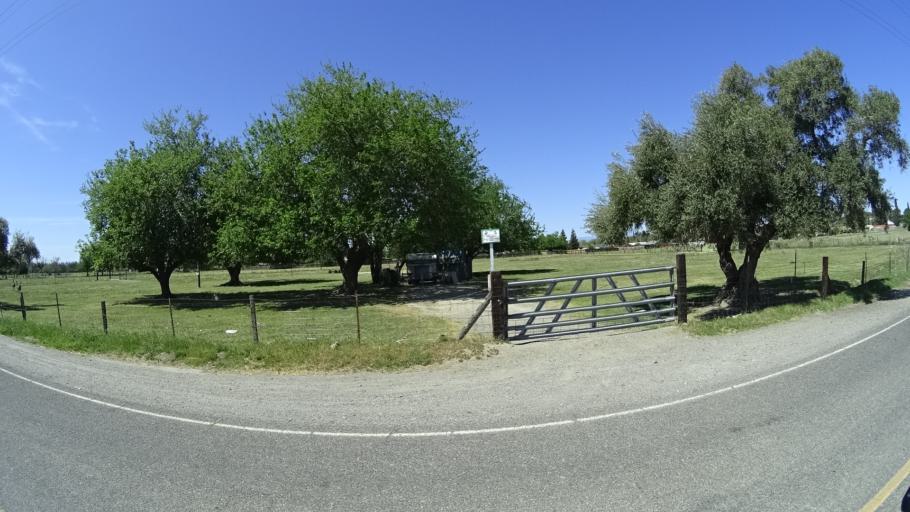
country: US
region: California
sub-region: Glenn County
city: Orland
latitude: 39.7377
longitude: -122.1781
